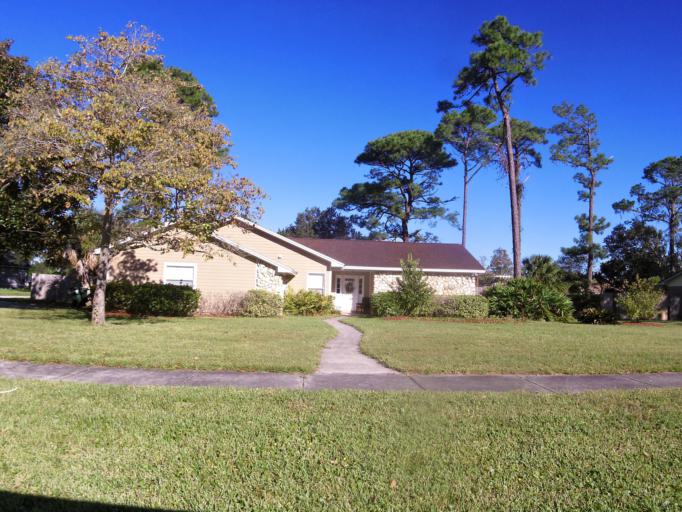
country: US
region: Florida
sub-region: Duval County
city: Neptune Beach
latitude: 30.3015
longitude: -81.4380
